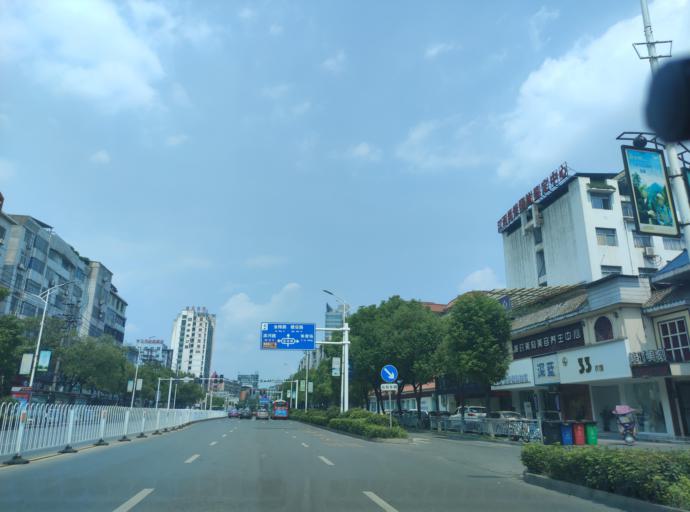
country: CN
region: Jiangxi Sheng
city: Pingxiang
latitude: 27.6401
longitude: 113.8611
